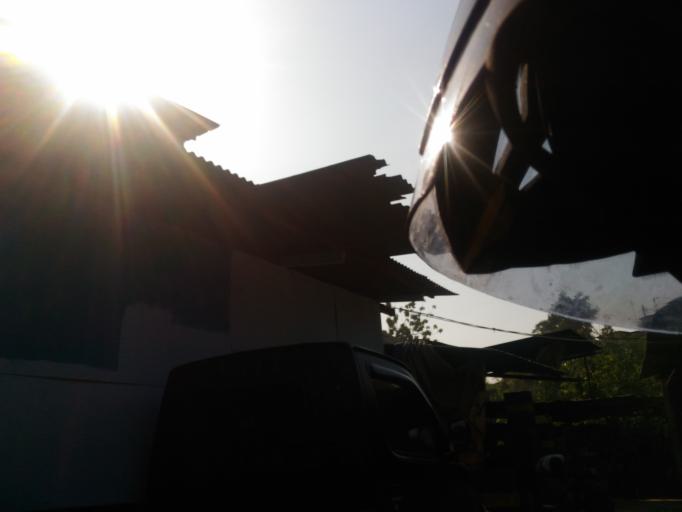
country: ID
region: West Java
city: Depok
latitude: -6.3416
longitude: 106.8384
